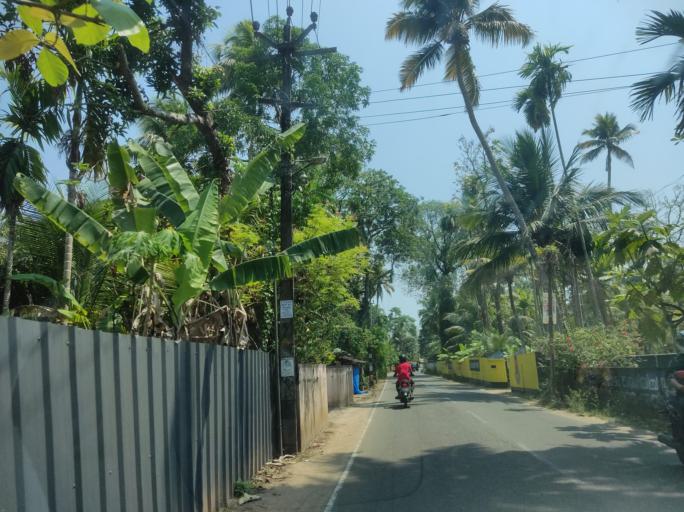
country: IN
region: Kerala
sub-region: Alappuzha
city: Kutiatodu
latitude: 9.7834
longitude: 76.3043
